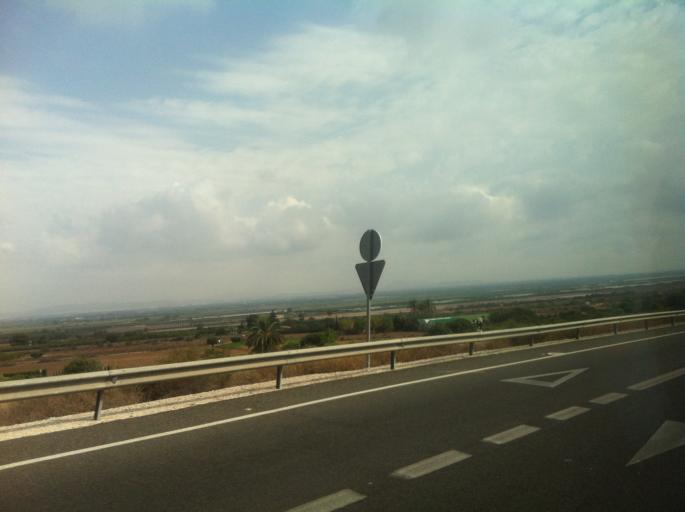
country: ES
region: Valencia
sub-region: Provincia de Alicante
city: Guardamar del Segura
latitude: 38.1577
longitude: -0.6549
